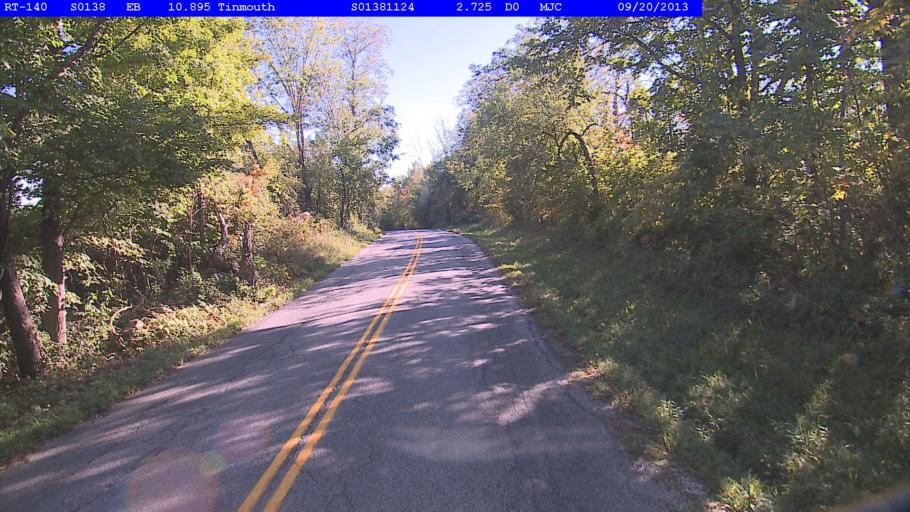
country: US
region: Vermont
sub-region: Rutland County
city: West Rutland
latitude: 43.4563
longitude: -73.0488
